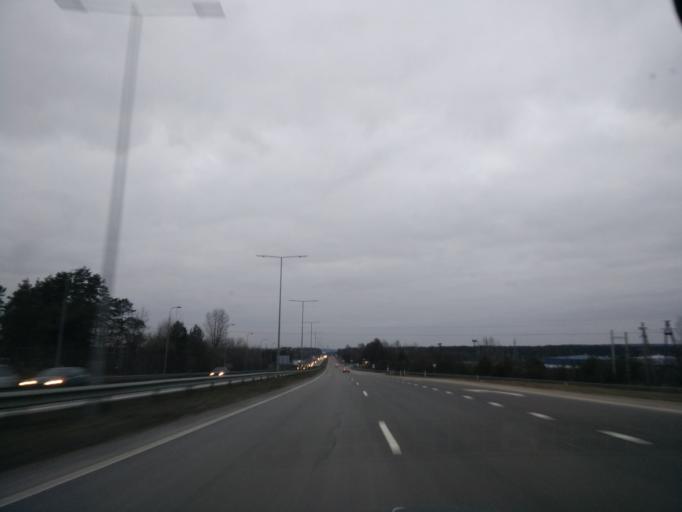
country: LT
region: Vilnius County
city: Pilaite
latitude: 54.6562
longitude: 25.1477
